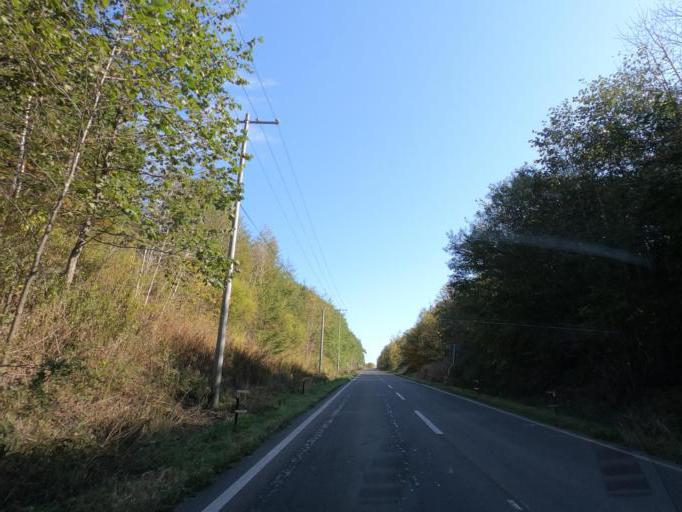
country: JP
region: Hokkaido
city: Otofuke
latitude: 42.9963
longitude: 143.2595
